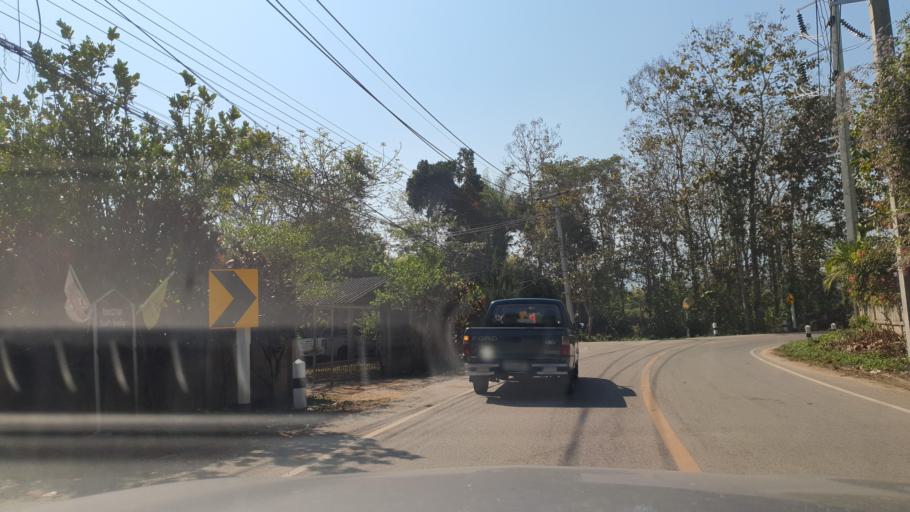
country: TH
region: Chiang Rai
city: Mae Lao
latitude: 19.7988
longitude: 99.7007
